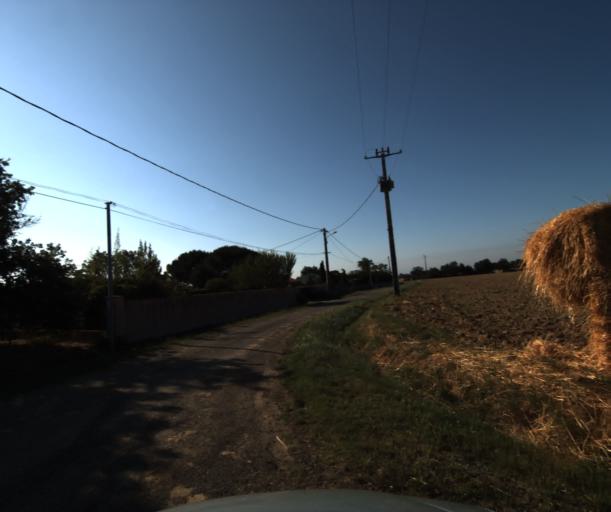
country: FR
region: Midi-Pyrenees
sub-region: Departement de la Haute-Garonne
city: Labarthe-sur-Leze
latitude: 43.4391
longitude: 1.3773
